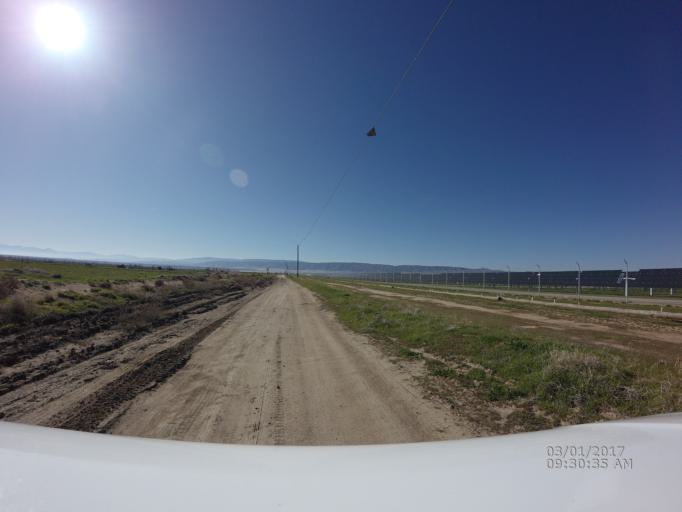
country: US
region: California
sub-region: Los Angeles County
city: Quartz Hill
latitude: 34.7172
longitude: -118.2721
